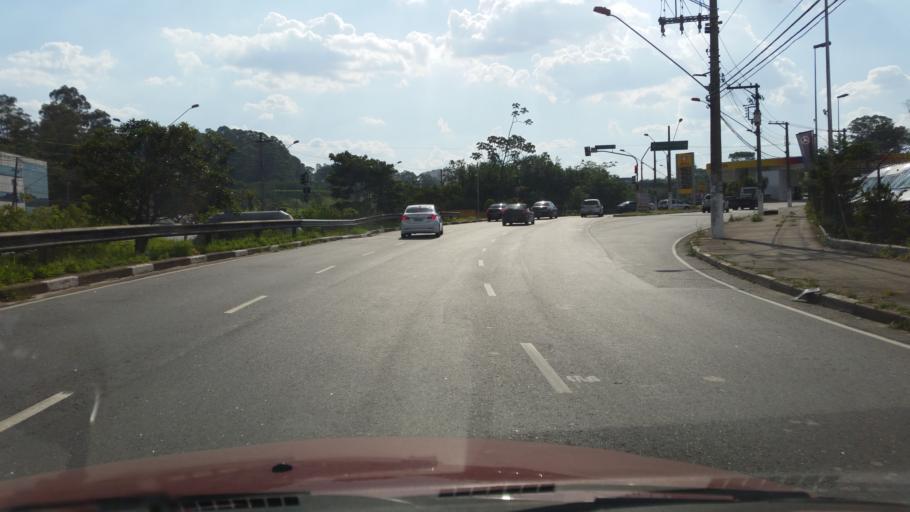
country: BR
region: Sao Paulo
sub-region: Diadema
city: Diadema
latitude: -23.6840
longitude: -46.6039
